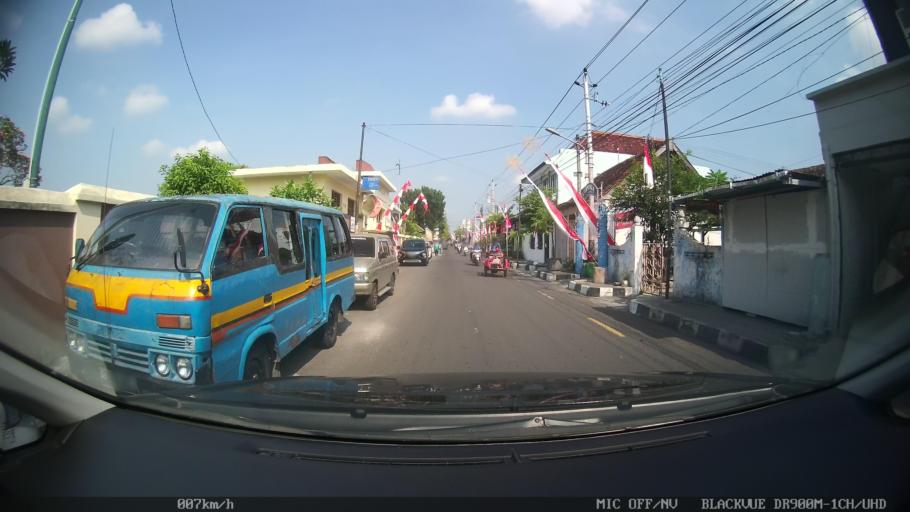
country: ID
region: Daerah Istimewa Yogyakarta
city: Yogyakarta
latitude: -7.8081
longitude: 110.3720
